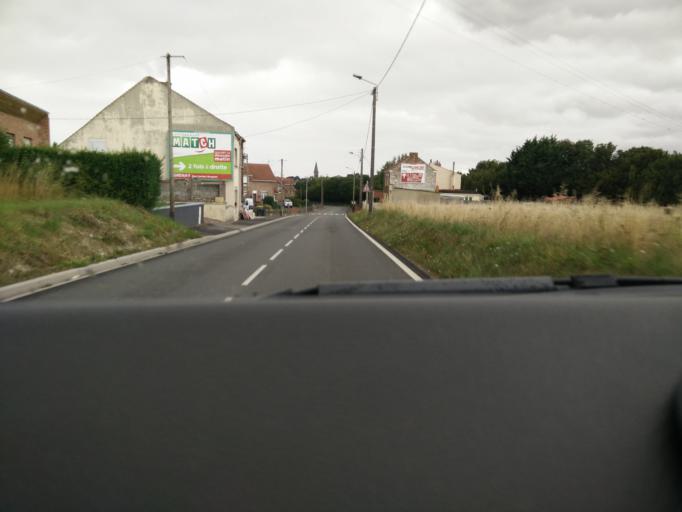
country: FR
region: Nord-Pas-de-Calais
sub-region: Departement du Pas-de-Calais
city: Grenay
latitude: 50.4437
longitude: 2.7423
